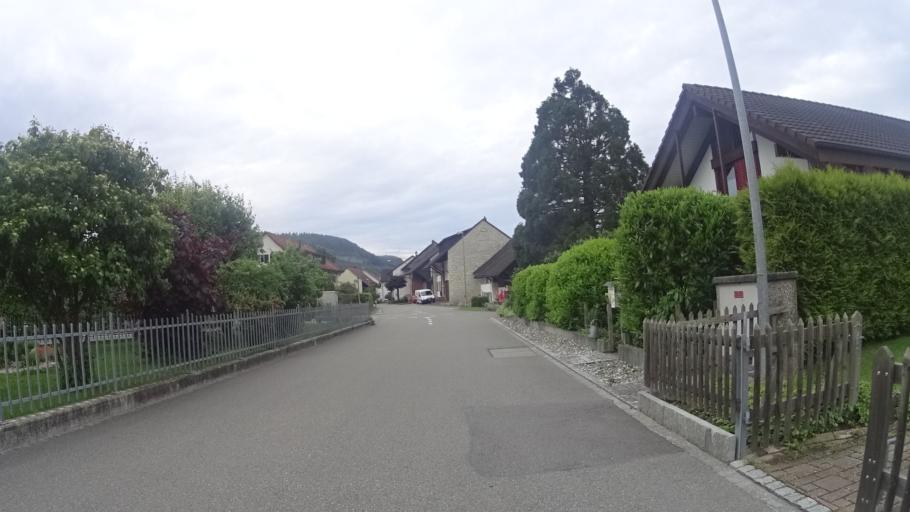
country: CH
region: Aargau
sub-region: Bezirk Baden
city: Wurenlingen
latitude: 47.5367
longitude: 8.2557
